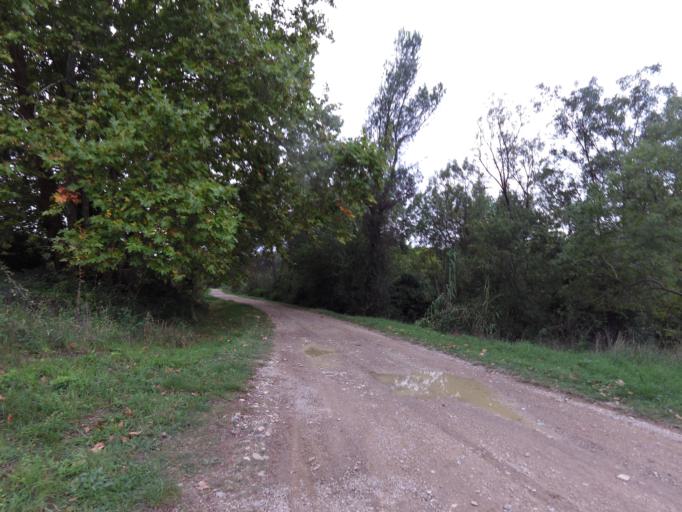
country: FR
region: Languedoc-Roussillon
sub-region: Departement de l'Herault
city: Villetelle
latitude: 43.7402
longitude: 4.1297
